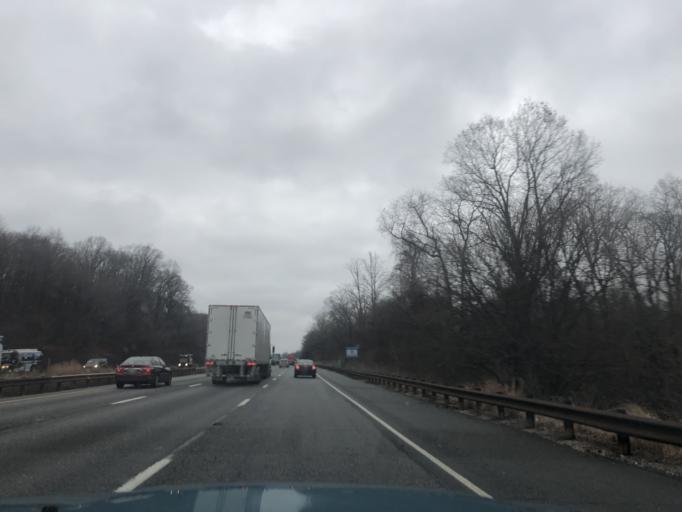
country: US
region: Pennsylvania
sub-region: Delaware County
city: Media
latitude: 39.9408
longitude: -75.3583
